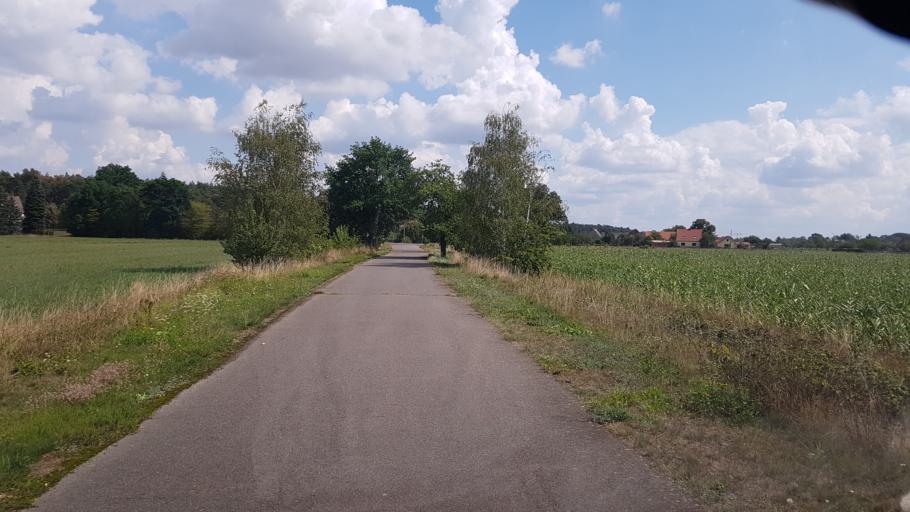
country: DE
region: Brandenburg
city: Calau
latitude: 51.7768
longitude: 13.9524
